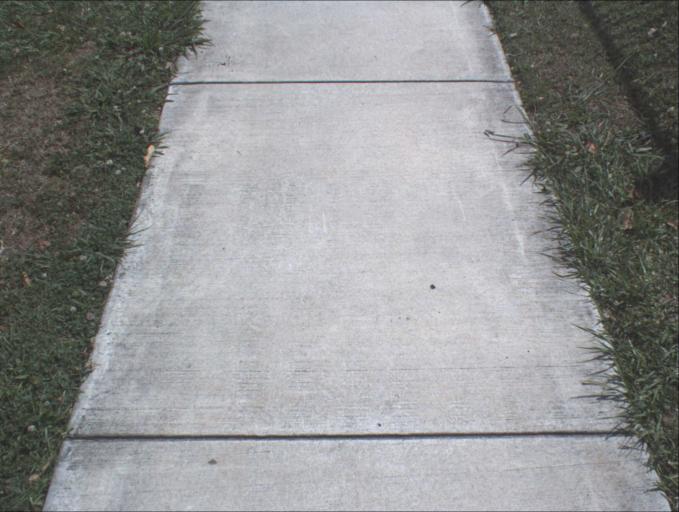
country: AU
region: Queensland
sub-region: Logan
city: Slacks Creek
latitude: -27.6618
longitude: 153.1434
